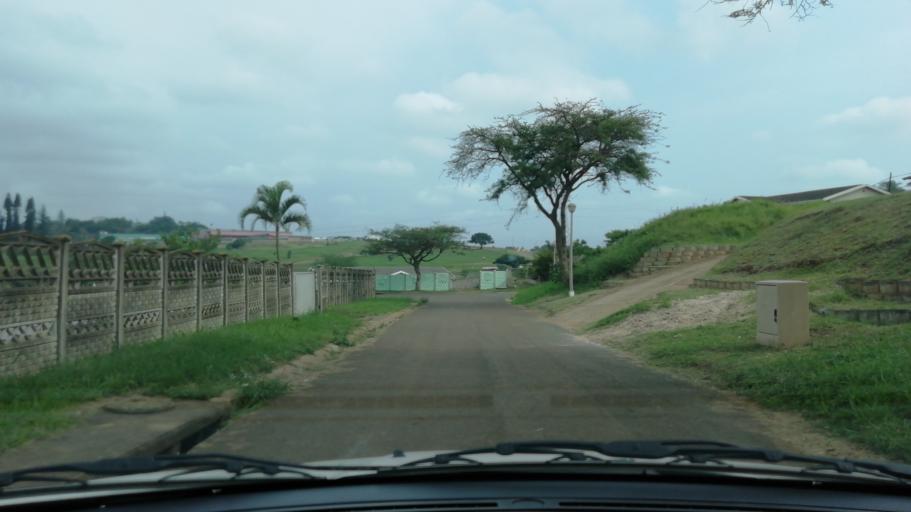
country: ZA
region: KwaZulu-Natal
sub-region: uThungulu District Municipality
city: Empangeni
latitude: -28.7406
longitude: 31.8808
